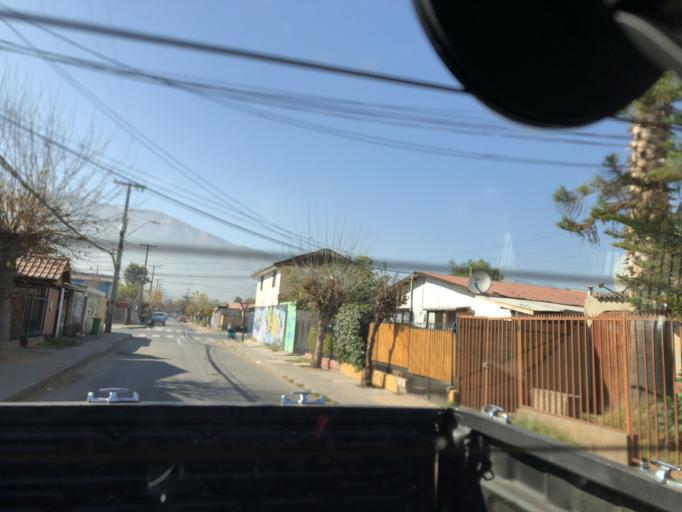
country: CL
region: Santiago Metropolitan
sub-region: Provincia de Cordillera
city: Puente Alto
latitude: -33.5696
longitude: -70.5731
